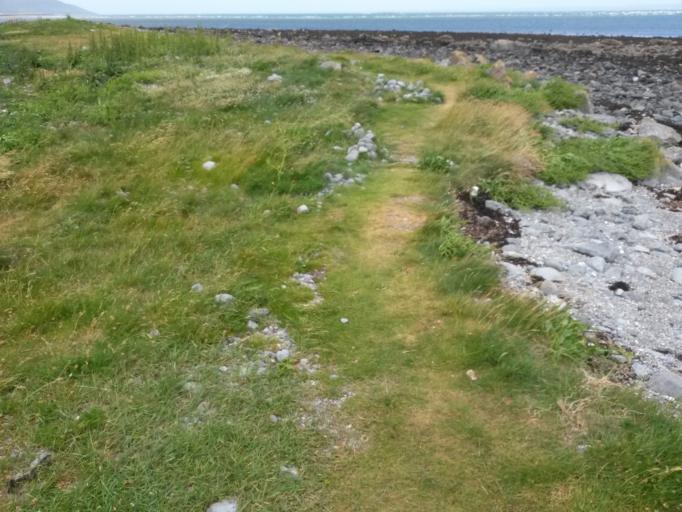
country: IE
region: Connaught
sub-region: County Galway
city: Bearna
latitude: 53.1304
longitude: -9.1293
